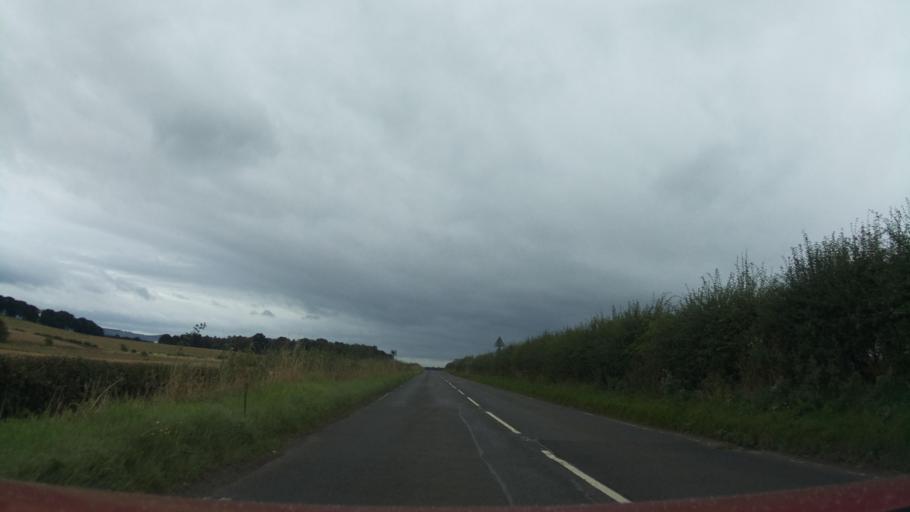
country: GB
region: Scotland
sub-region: Perth and Kinross
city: Milnathort
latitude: 56.2236
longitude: -3.4458
